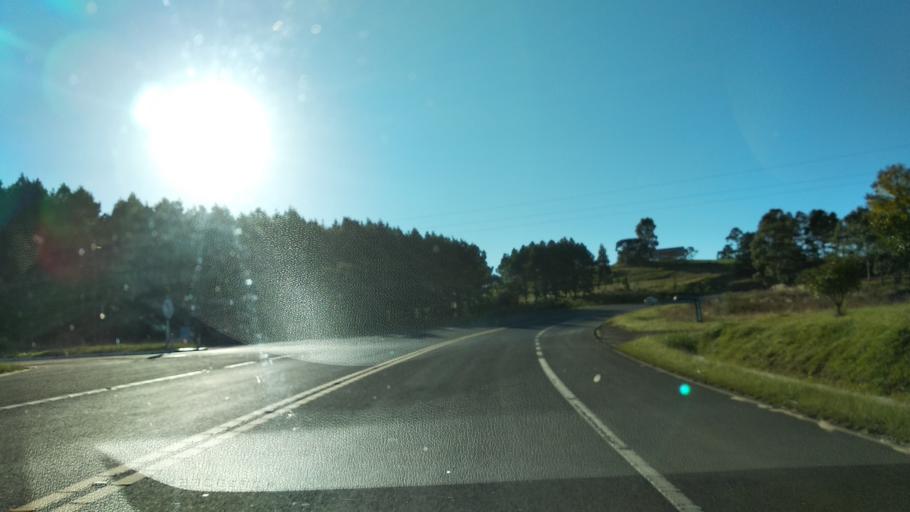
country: BR
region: Santa Catarina
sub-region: Lages
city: Lages
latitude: -27.7900
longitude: -50.4105
